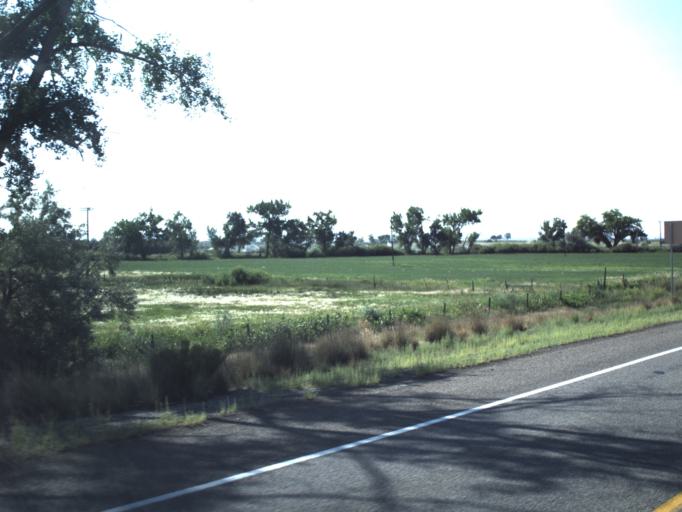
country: US
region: Utah
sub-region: Emery County
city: Castle Dale
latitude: 39.2084
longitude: -111.0243
